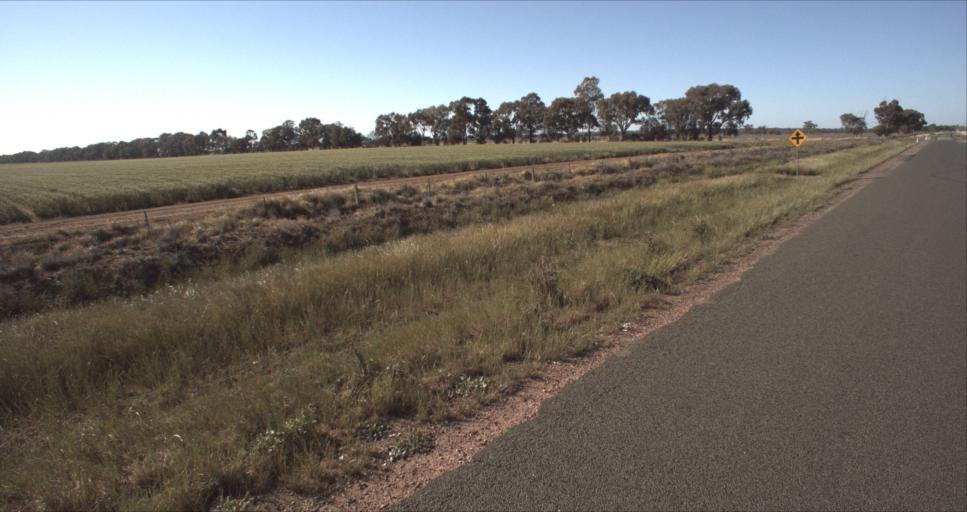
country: AU
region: New South Wales
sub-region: Leeton
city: Leeton
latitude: -34.5761
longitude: 146.2625
